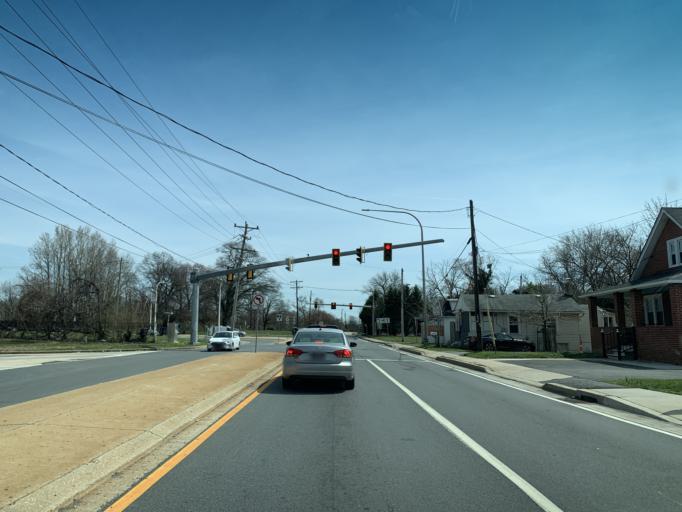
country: US
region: Delaware
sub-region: New Castle County
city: Newport
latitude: 39.7259
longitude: -75.6193
